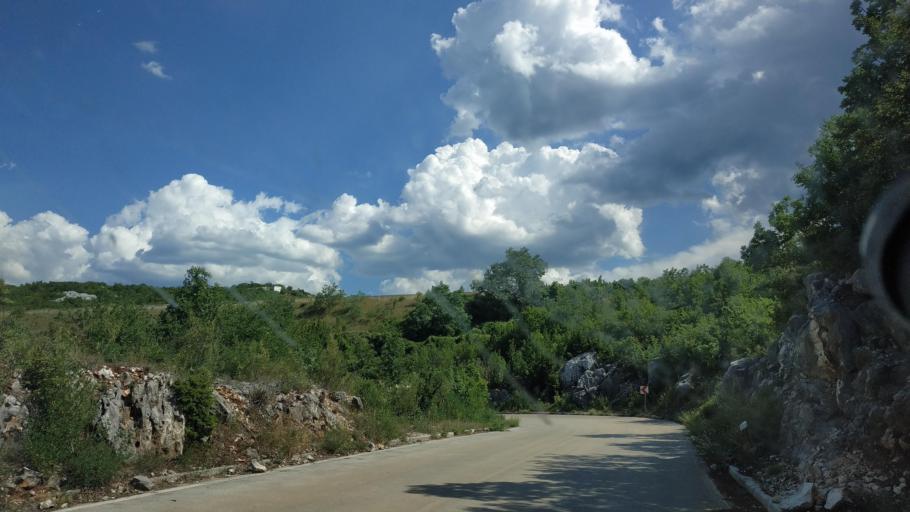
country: HR
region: Splitsko-Dalmatinska
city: Dugopolje
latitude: 43.5833
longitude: 16.6536
